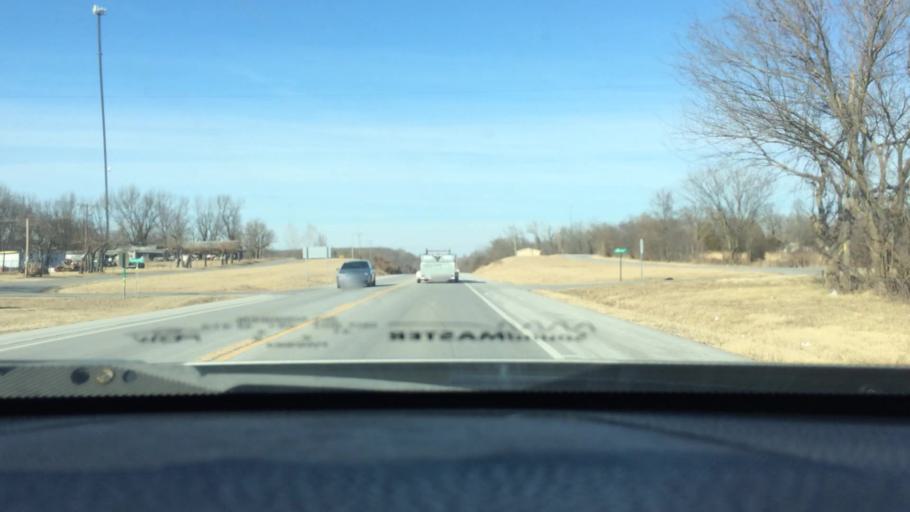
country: US
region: Missouri
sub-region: Newton County
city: Neosho
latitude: 36.8911
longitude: -94.3170
